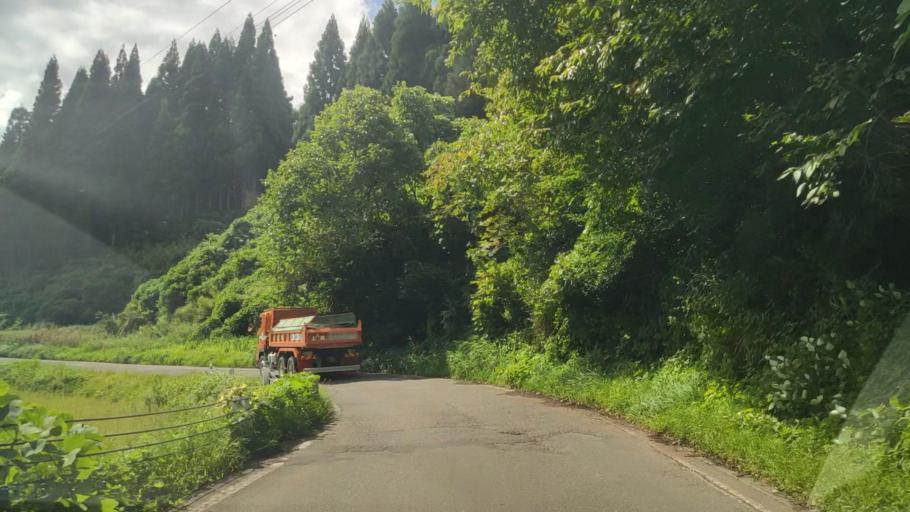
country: JP
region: Niigata
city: Arai
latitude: 36.9434
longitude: 138.2909
